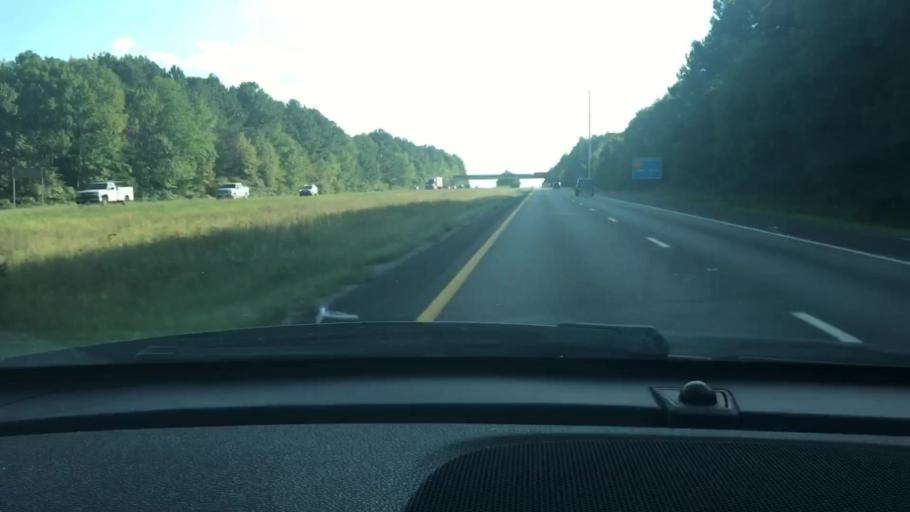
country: US
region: Tennessee
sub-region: Sumner County
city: White House
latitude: 36.4395
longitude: -86.7048
